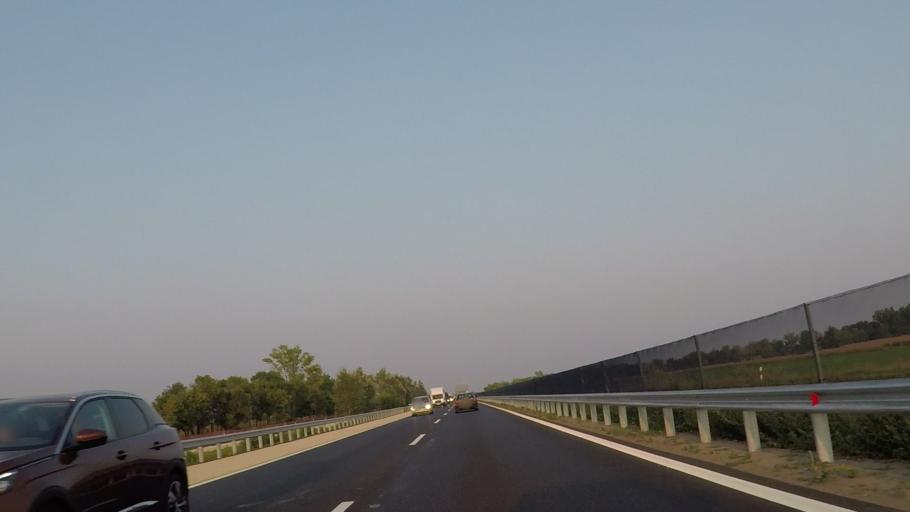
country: HU
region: Pest
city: Cegled
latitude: 47.1908
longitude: 19.8792
